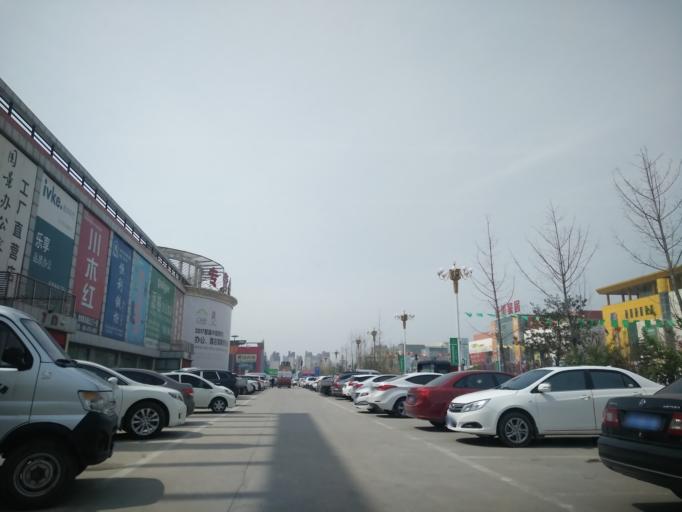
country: CN
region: Tianjin Shi
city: Xiawuqi
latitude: 39.7493
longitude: 117.0177
